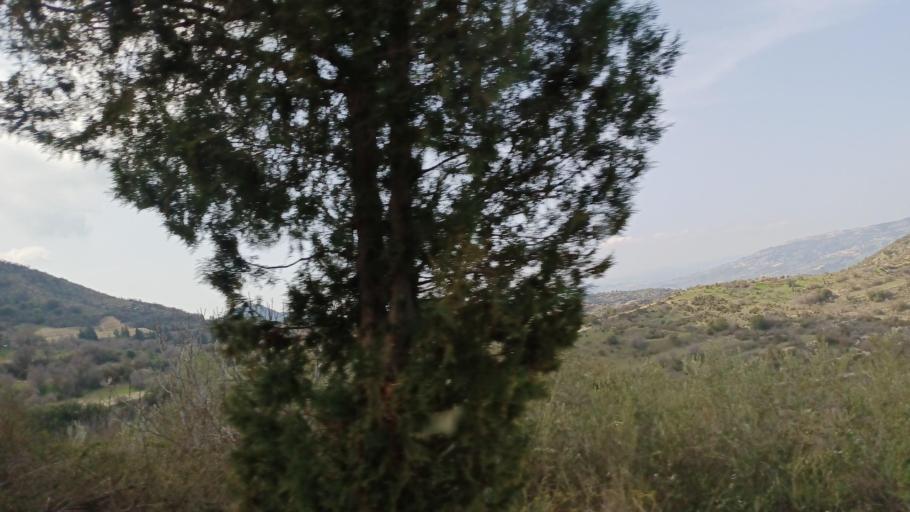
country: CY
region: Limassol
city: Pachna
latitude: 34.7820
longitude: 32.7362
